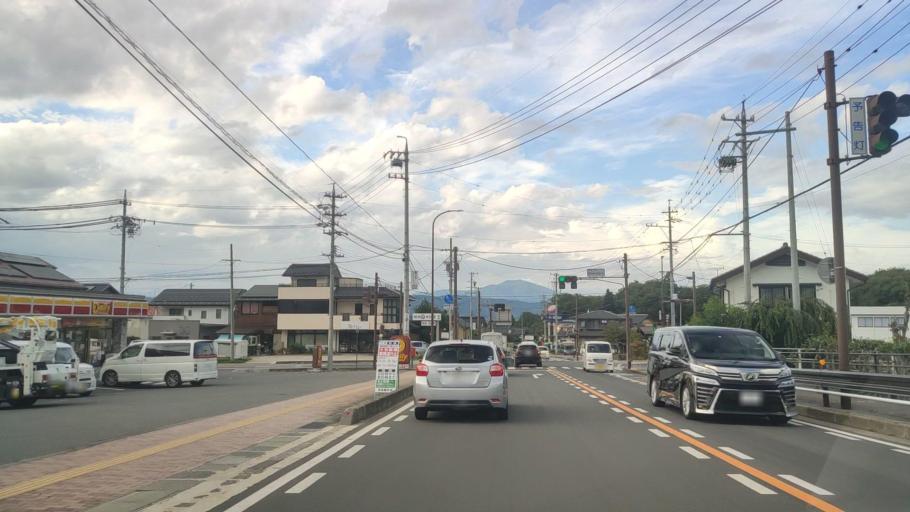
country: JP
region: Nagano
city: Suzaka
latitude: 36.6898
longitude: 138.3157
